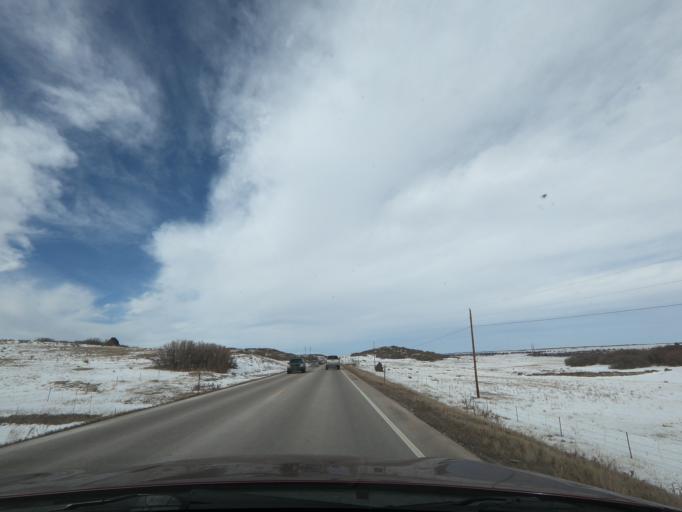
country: US
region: Colorado
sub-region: Douglas County
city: Castle Rock
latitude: 39.2768
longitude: -104.7370
